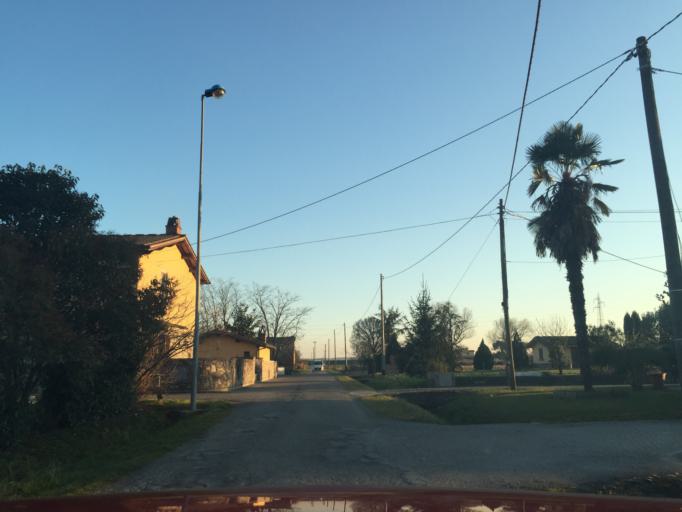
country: IT
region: Tuscany
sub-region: Provincia di Pistoia
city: Ponte Buggianese
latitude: 43.8406
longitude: 10.7576
